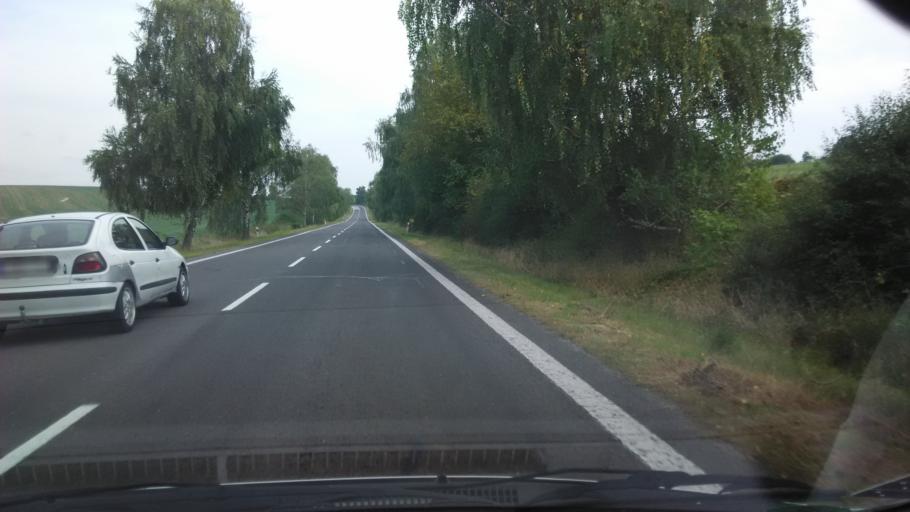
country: SK
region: Nitriansky
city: Zeliezovce
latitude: 48.1262
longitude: 18.7157
